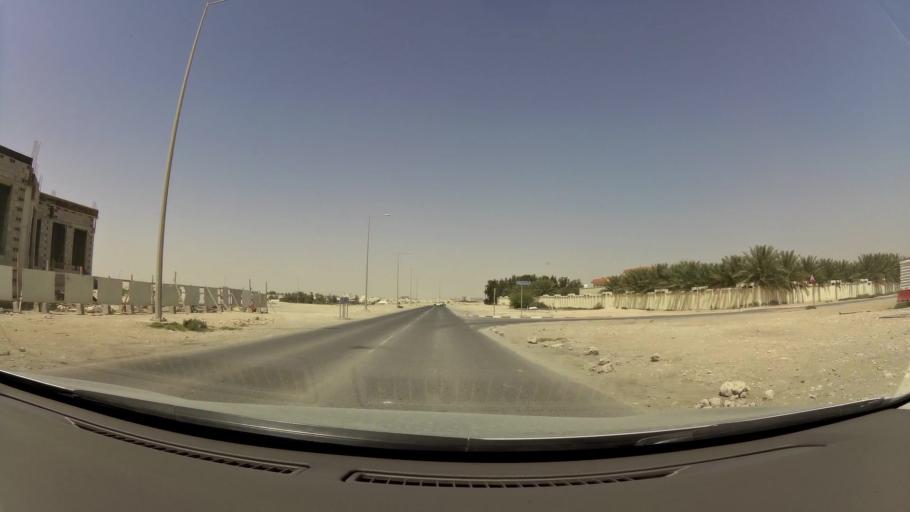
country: QA
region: Baladiyat ar Rayyan
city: Ar Rayyan
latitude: 25.2541
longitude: 51.4024
